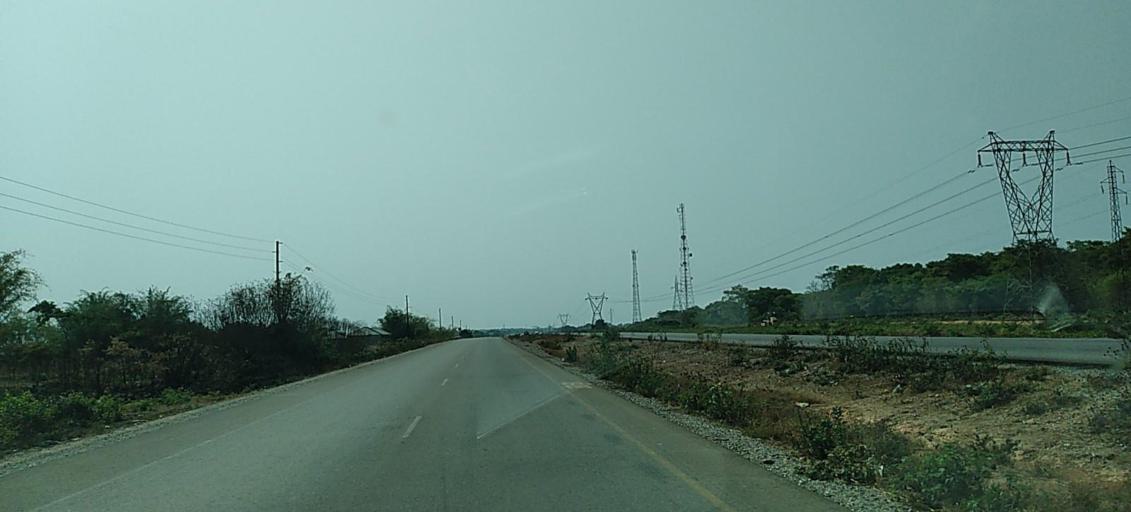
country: ZM
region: Copperbelt
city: Chingola
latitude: -12.5930
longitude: 27.9519
